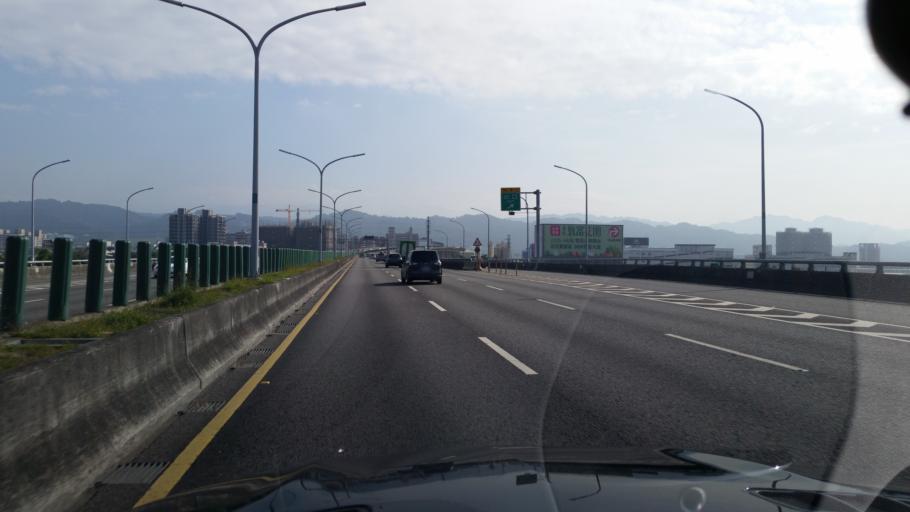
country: TW
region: Taiwan
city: Fengyuan
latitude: 24.2009
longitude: 120.6975
